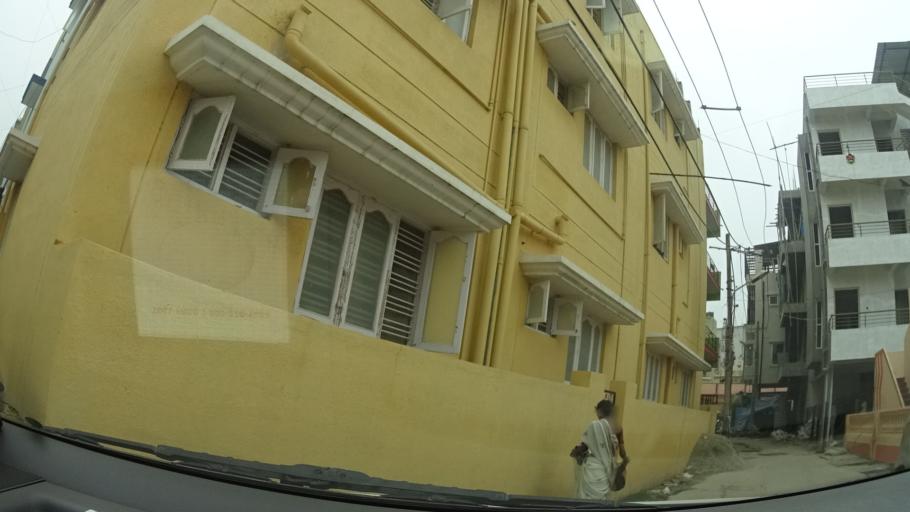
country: IN
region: Karnataka
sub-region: Bangalore Urban
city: Bangalore
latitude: 13.0352
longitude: 77.6337
